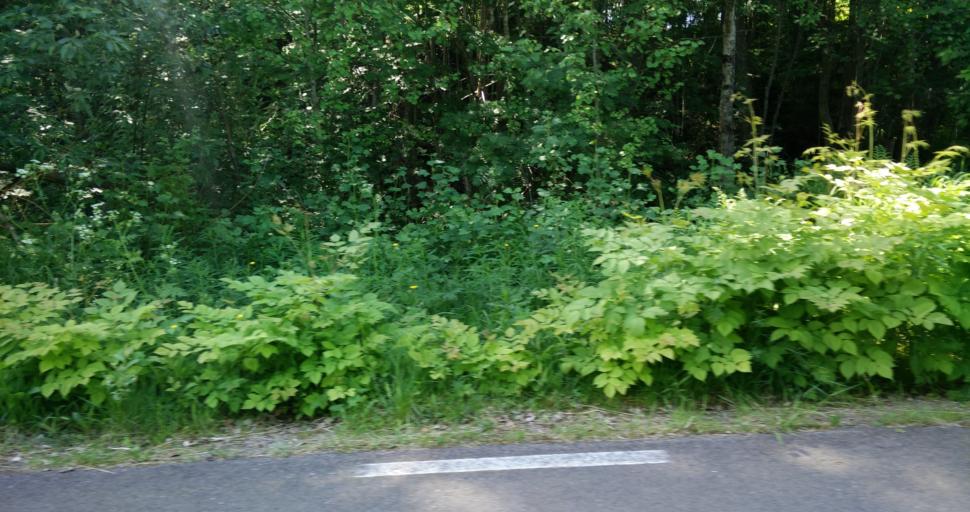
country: SE
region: Vaermland
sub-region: Hagfors Kommun
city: Hagfors
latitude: 60.0000
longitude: 13.6002
